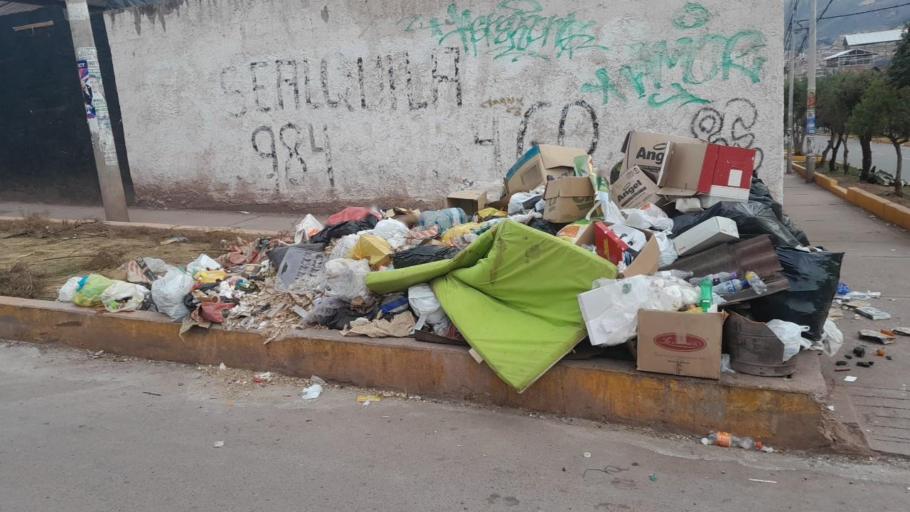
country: PE
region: Cusco
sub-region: Provincia de Cusco
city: Saylla
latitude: -13.5330
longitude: -71.9030
